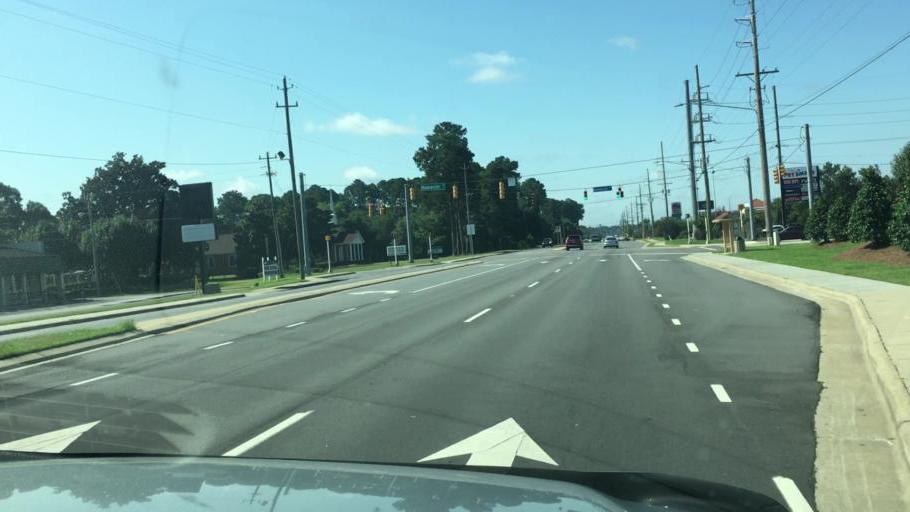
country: US
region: North Carolina
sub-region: Cumberland County
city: Fayetteville
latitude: 35.1269
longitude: -78.8793
